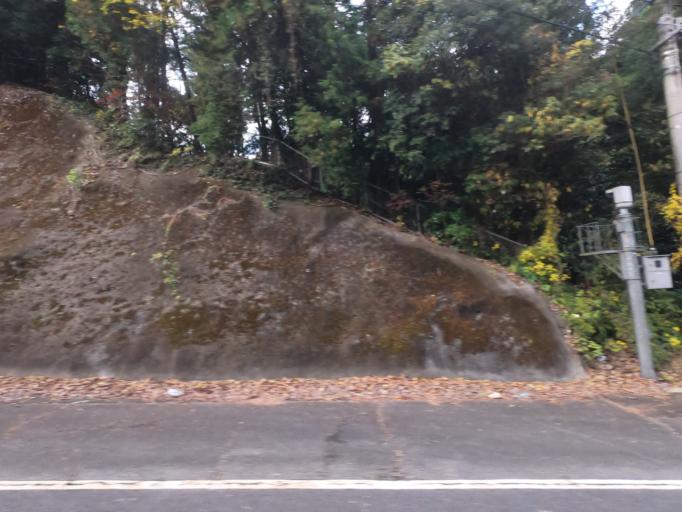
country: JP
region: Kumamoto
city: Minamata
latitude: 32.2469
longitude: 130.4940
